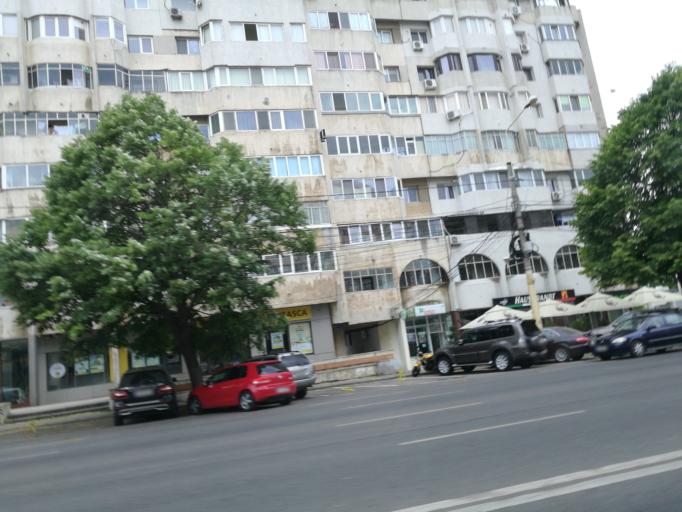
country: RO
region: Constanta
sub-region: Municipiul Constanta
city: Constanta
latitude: 44.1880
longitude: 28.6343
